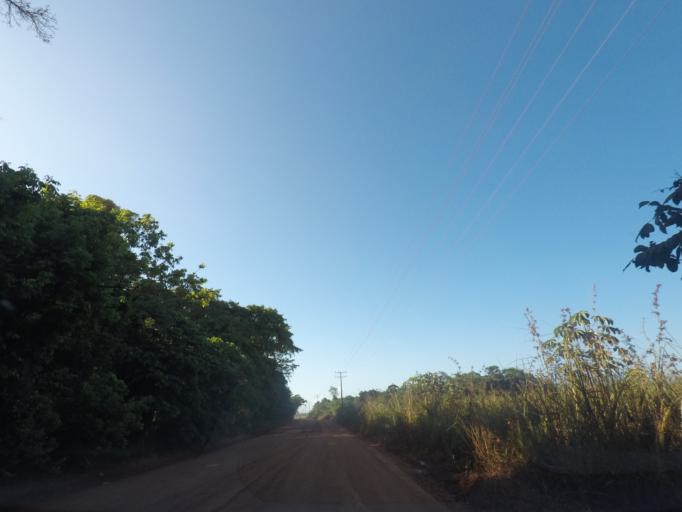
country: BR
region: Bahia
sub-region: Camamu
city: Camamu
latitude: -13.9457
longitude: -38.9467
